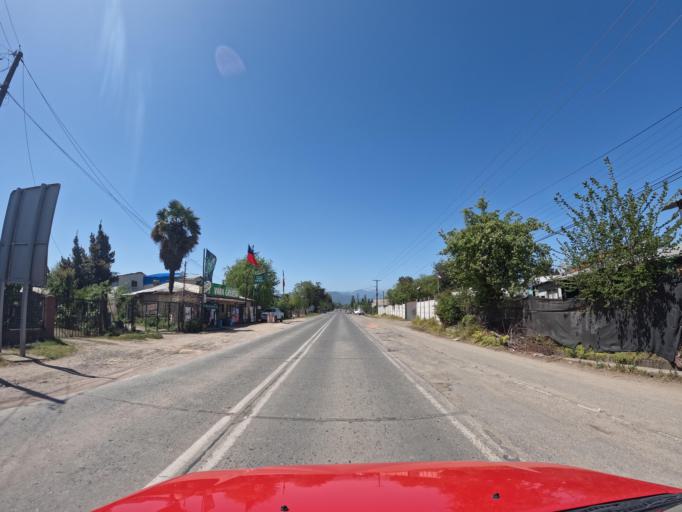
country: CL
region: Maule
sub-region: Provincia de Linares
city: Linares
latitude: -35.8301
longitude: -71.5113
